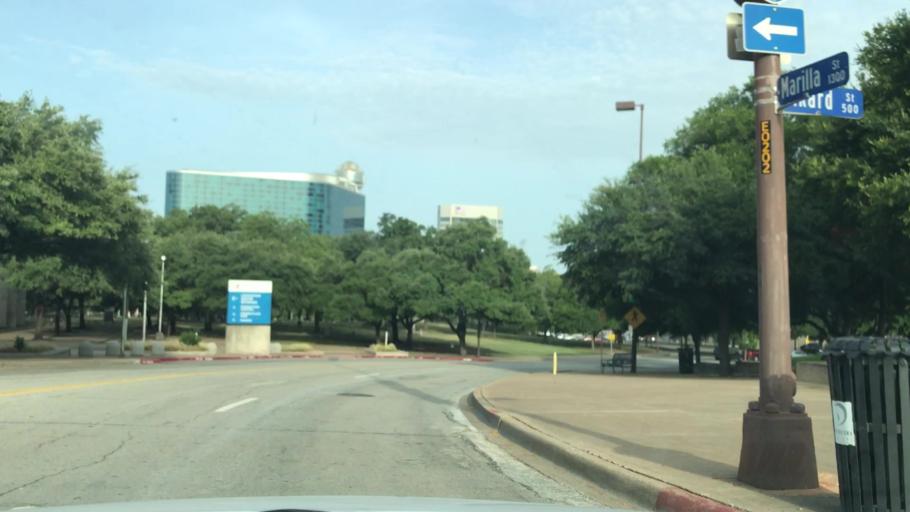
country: US
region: Texas
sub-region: Dallas County
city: Dallas
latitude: 32.7764
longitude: -96.7985
